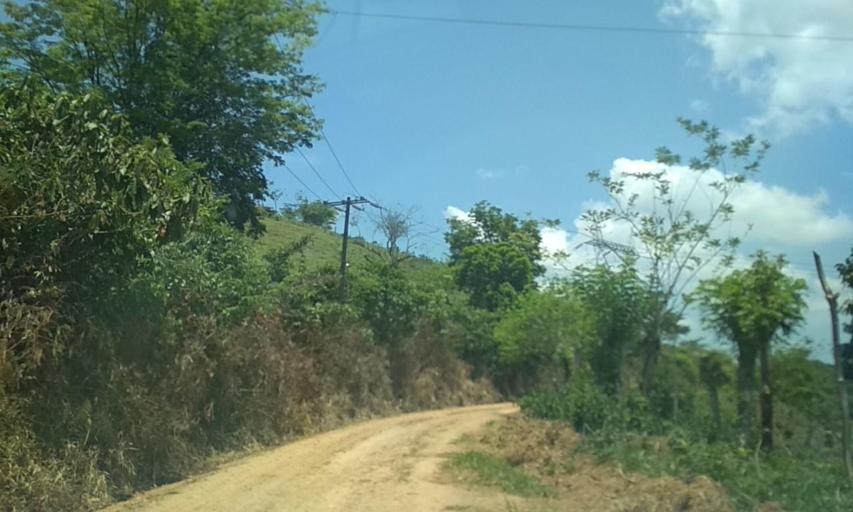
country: MX
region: Chiapas
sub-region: Tecpatan
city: Raudales Malpaso
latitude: 17.3913
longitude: -93.7361
